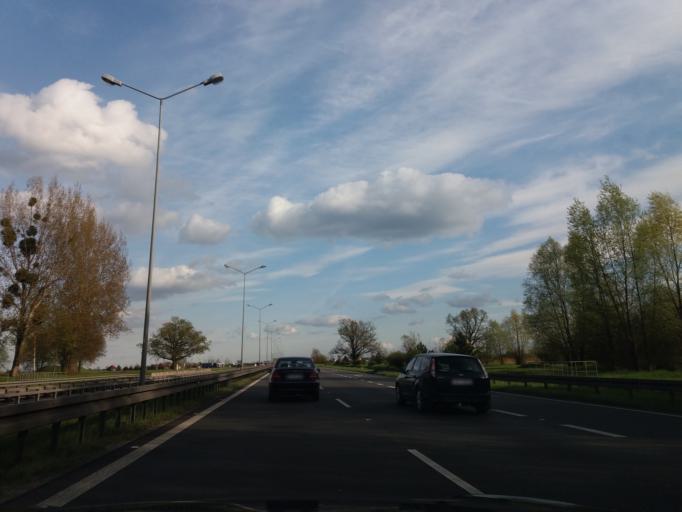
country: PL
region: Lower Silesian Voivodeship
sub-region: Powiat wroclawski
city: Zorawina
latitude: 50.9596
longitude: 17.0730
